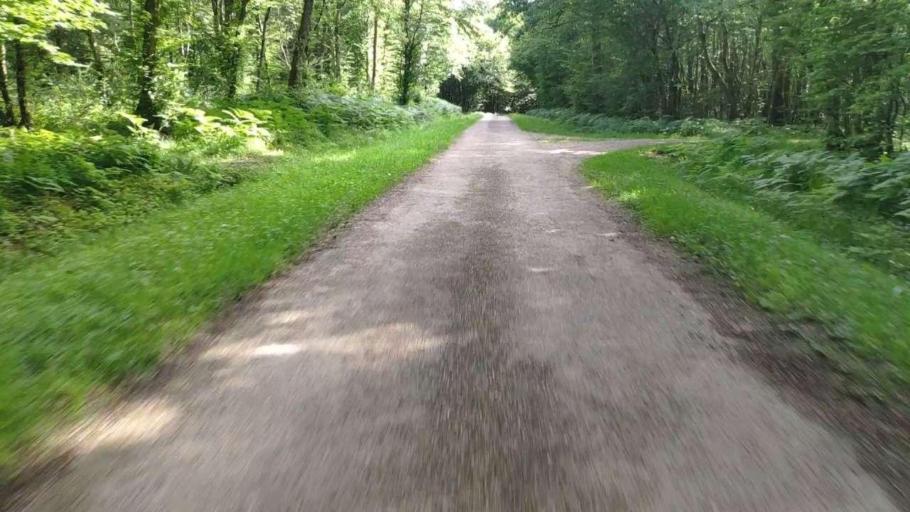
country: FR
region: Franche-Comte
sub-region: Departement du Jura
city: Bletterans
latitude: 46.8164
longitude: 5.5182
